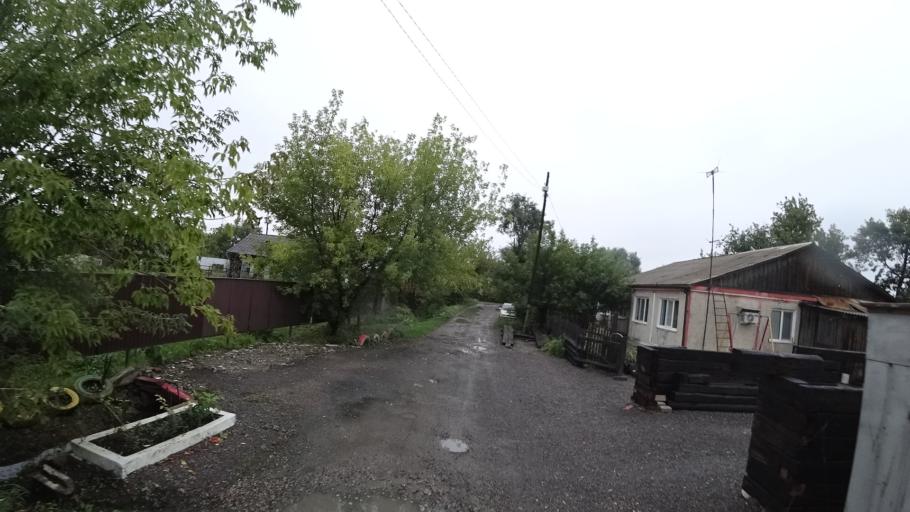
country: RU
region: Primorskiy
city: Chernigovka
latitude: 44.3373
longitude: 132.5716
